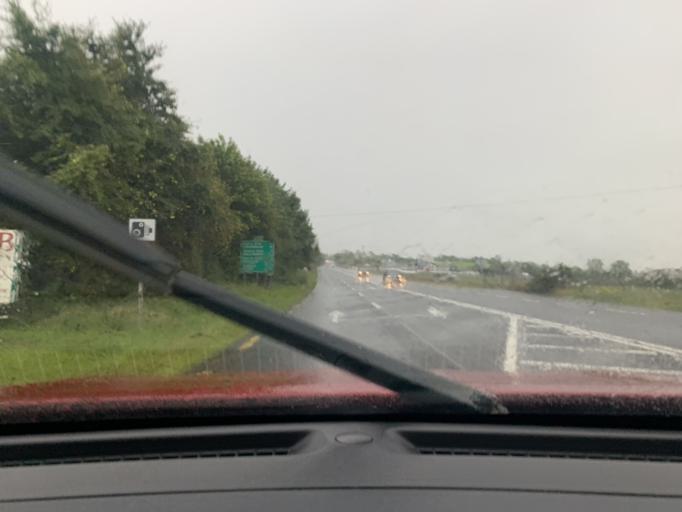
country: IE
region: Ulster
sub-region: County Donegal
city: Letterkenny
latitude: 54.9412
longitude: -7.6960
